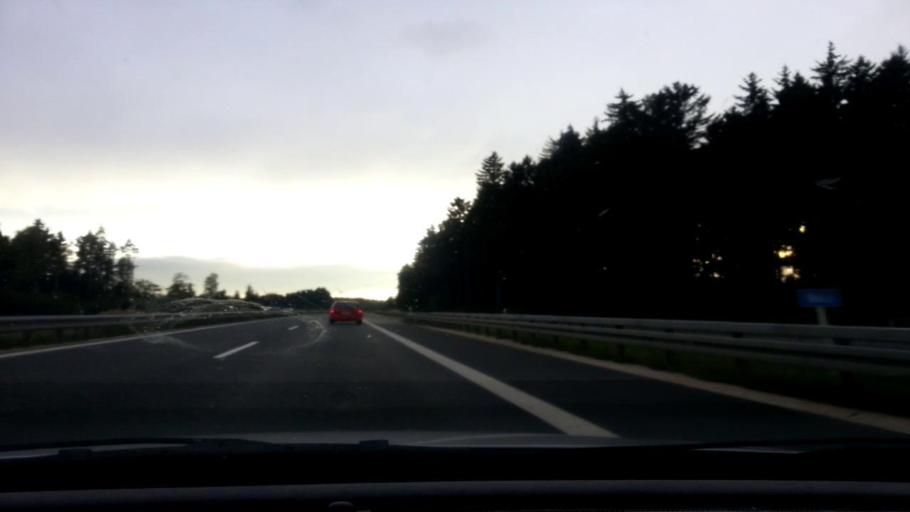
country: DE
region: Bavaria
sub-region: Upper Franconia
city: Stadelhofen
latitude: 49.9940
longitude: 11.1649
